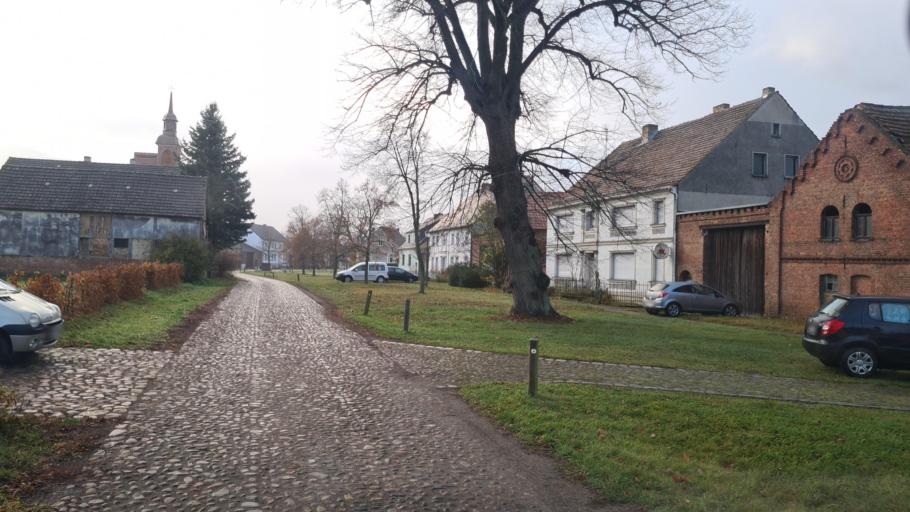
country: DE
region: Brandenburg
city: Beelitz
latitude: 52.1576
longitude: 12.9691
